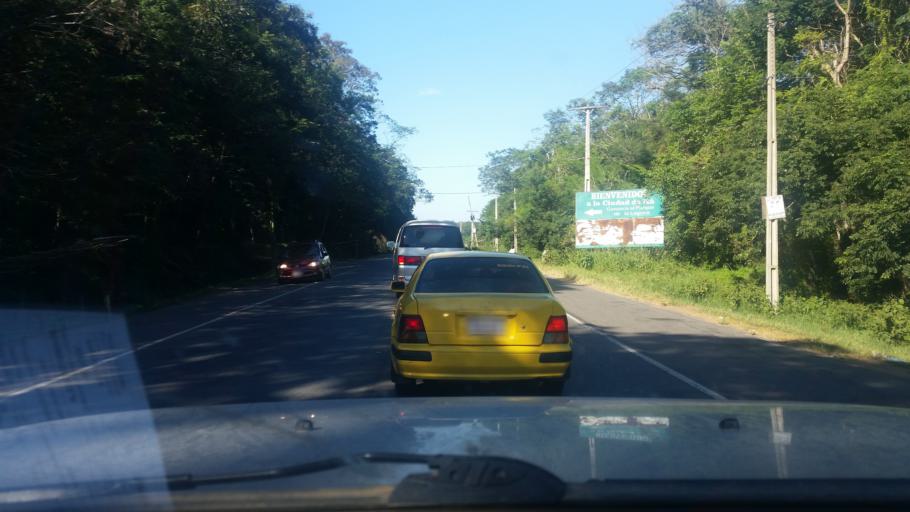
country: PY
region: Central
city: Ita
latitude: -25.5218
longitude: -57.3698
